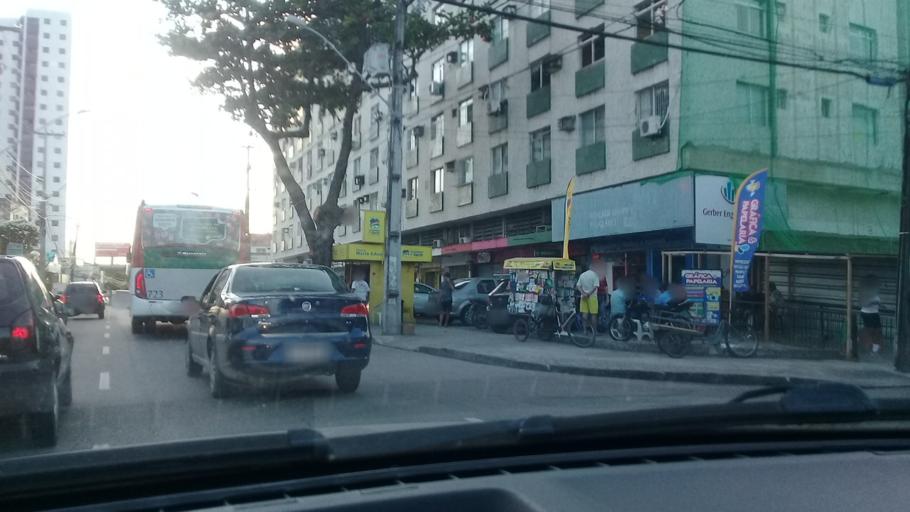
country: BR
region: Pernambuco
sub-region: Recife
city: Recife
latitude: -8.1324
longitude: -34.9082
